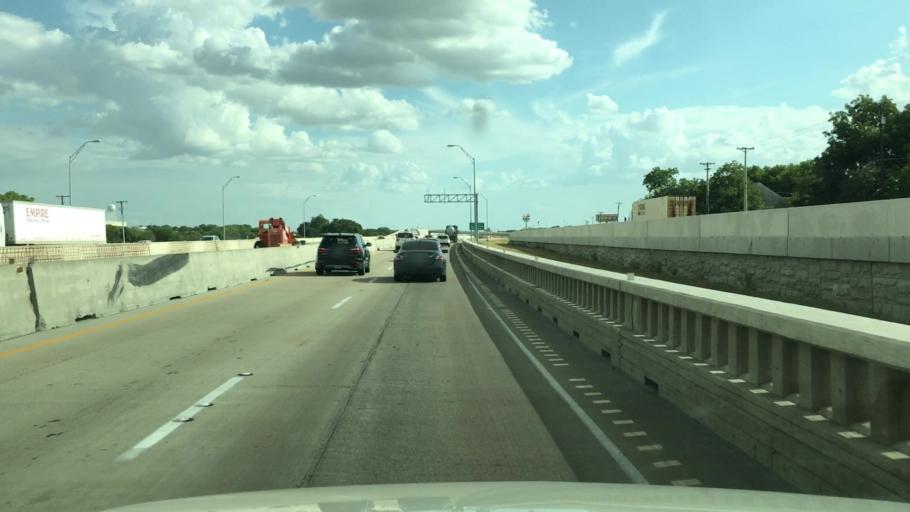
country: US
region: Texas
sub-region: Bell County
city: Troy
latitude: 31.2029
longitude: -97.3047
